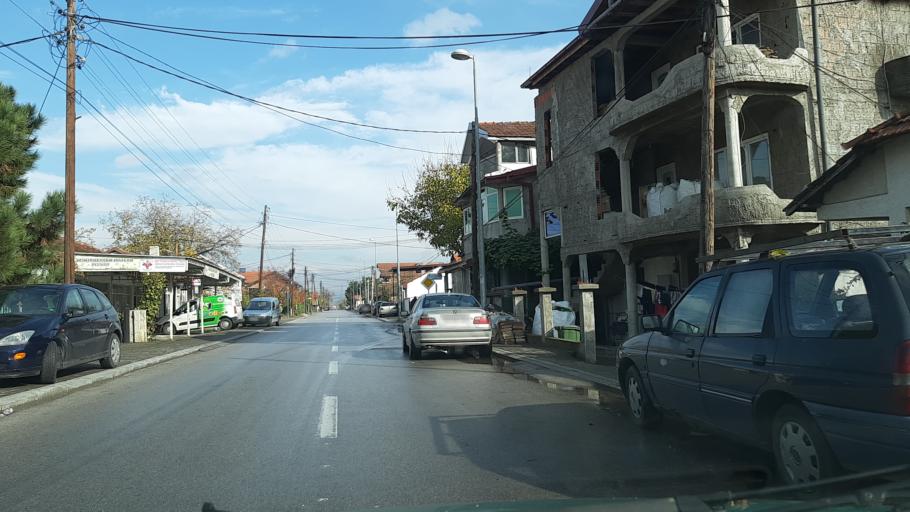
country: MK
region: Kisela Voda
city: Usje
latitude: 41.9787
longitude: 21.4860
